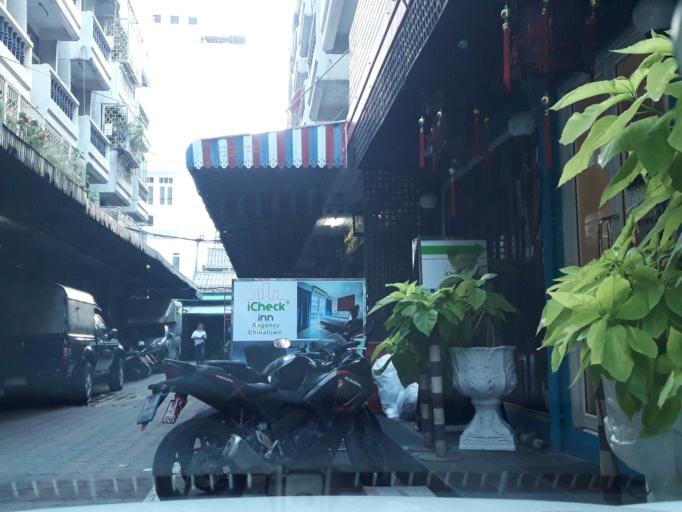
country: TH
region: Bangkok
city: Khlong San
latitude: 13.7426
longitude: 100.5082
